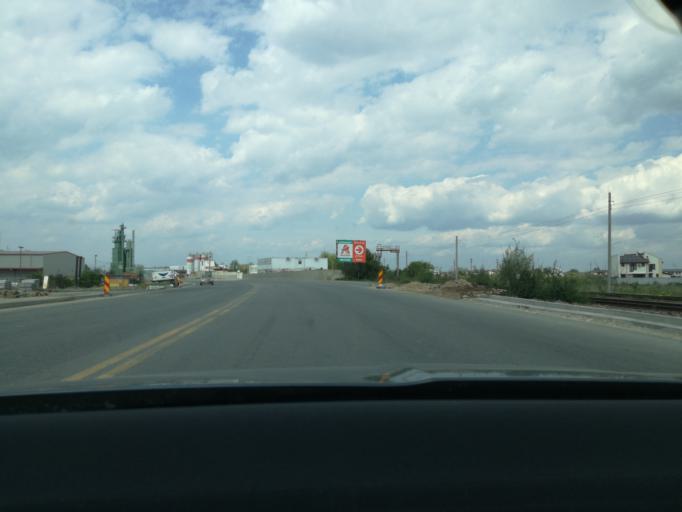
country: RO
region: Ilfov
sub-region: Comuna Chiajna
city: Chiajna
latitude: 44.4483
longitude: 25.9656
